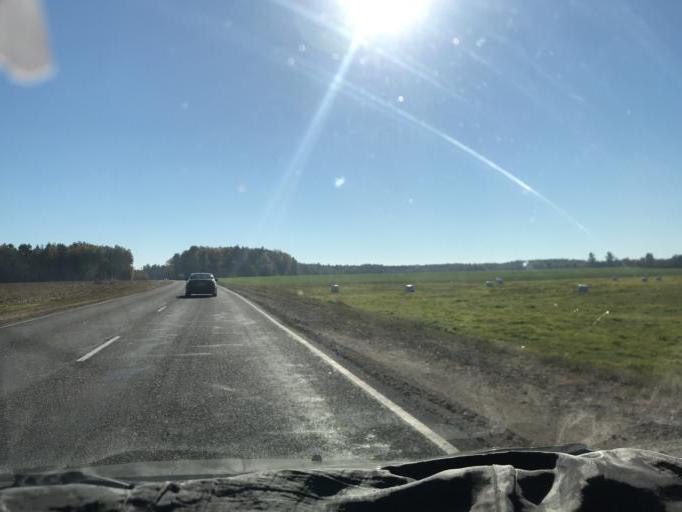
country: BY
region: Mogilev
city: Babruysk
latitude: 53.0610
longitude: 29.0845
